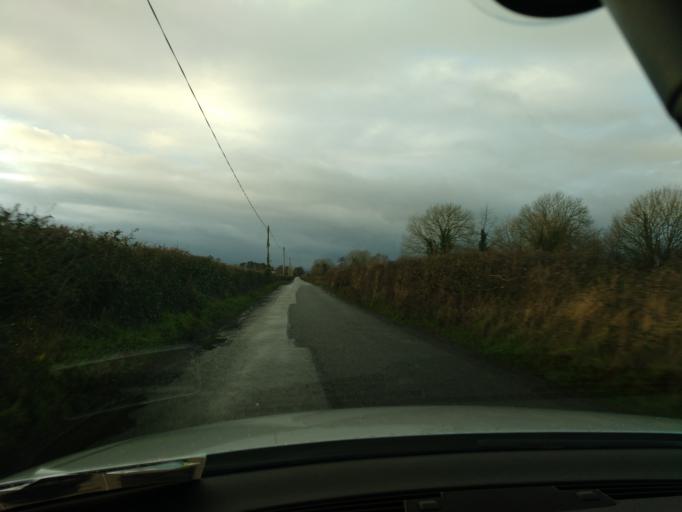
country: IE
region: Munster
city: Thurles
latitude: 52.6340
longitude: -7.8144
